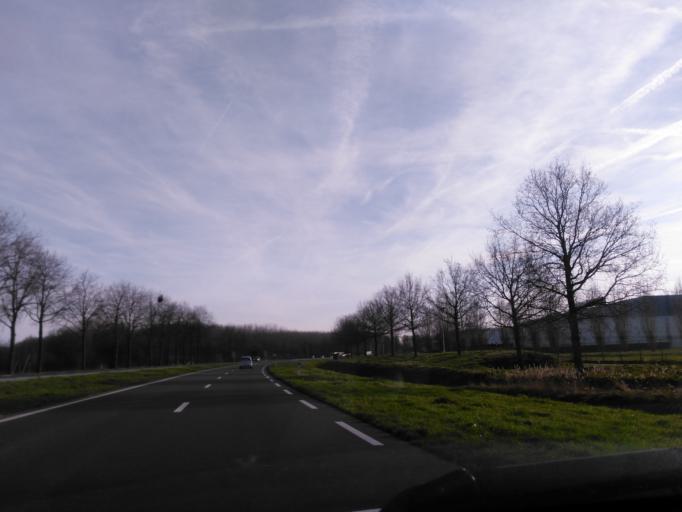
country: NL
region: Zeeland
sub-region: Gemeente Hulst
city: Hulst
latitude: 51.2680
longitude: 4.0542
